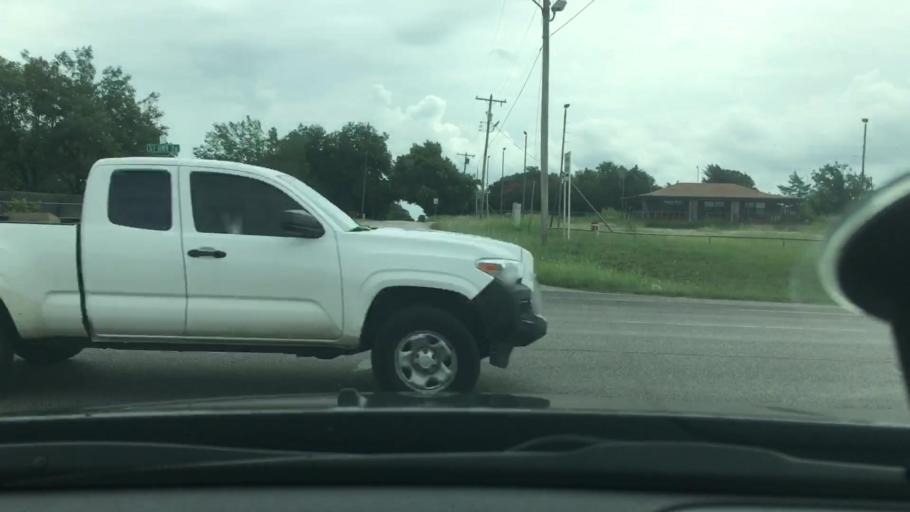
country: US
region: Oklahoma
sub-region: Carter County
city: Healdton
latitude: 34.2164
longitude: -97.4749
